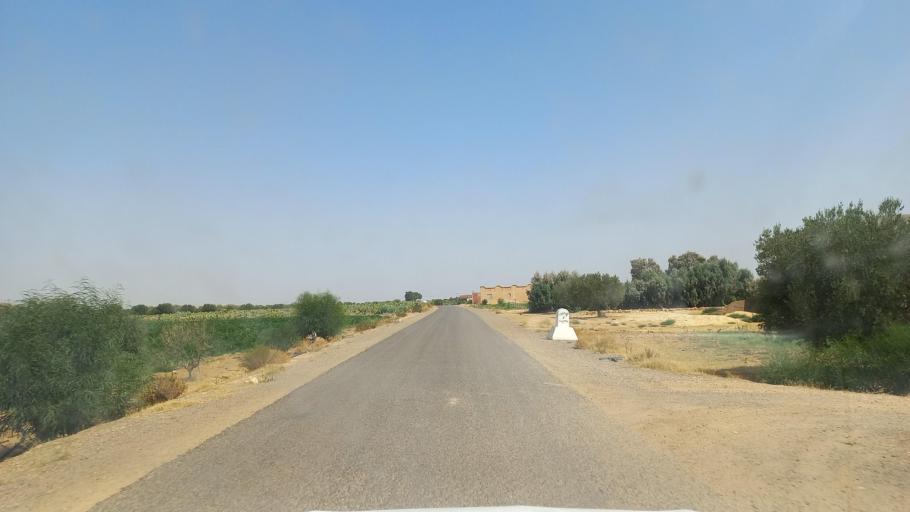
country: TN
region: Al Qasrayn
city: Kasserine
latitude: 35.2353
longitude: 9.0393
